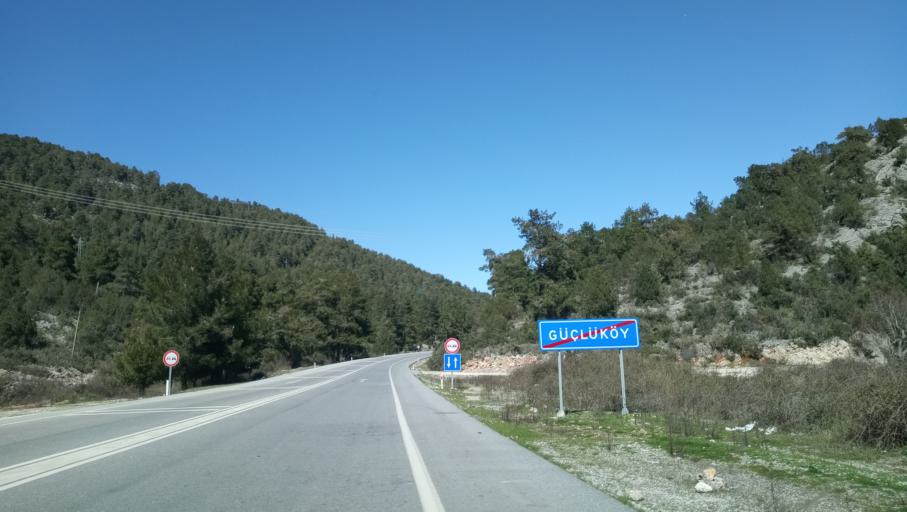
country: TR
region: Antalya
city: Guzelsu
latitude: 36.8326
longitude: 31.7869
